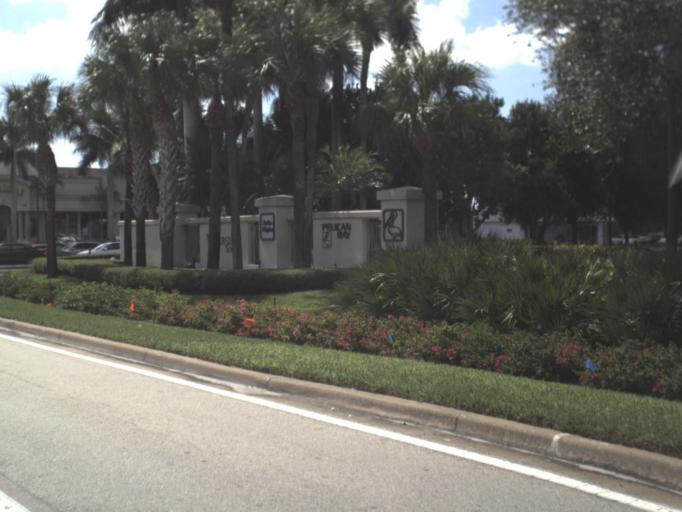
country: US
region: Florida
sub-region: Collier County
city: Pine Ridge
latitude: 26.2119
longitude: -81.8006
